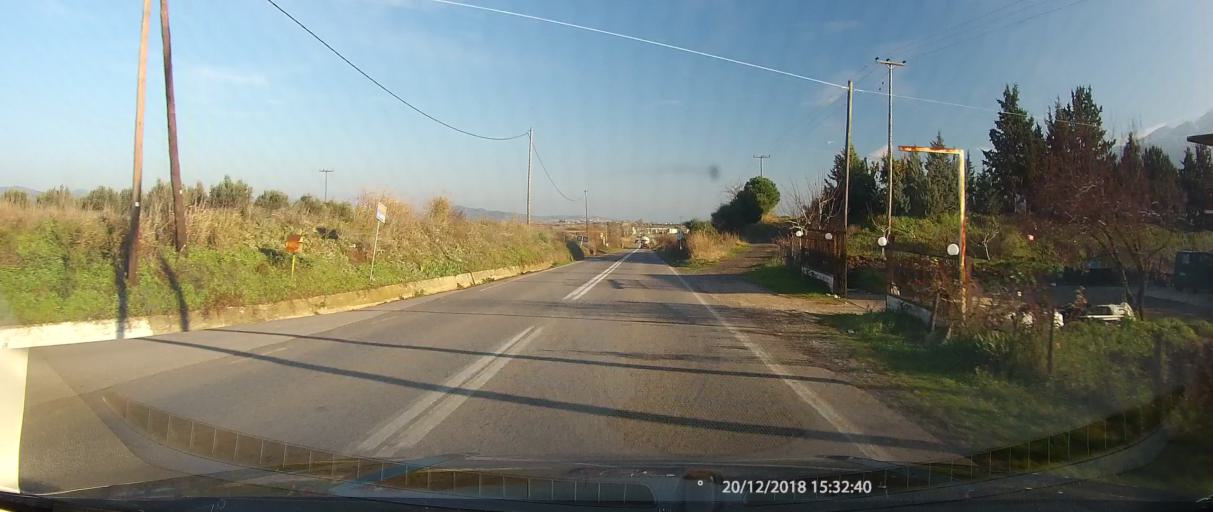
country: GR
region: Central Greece
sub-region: Nomos Fthiotidos
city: Lianokladhion
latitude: 38.9284
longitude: 22.2617
